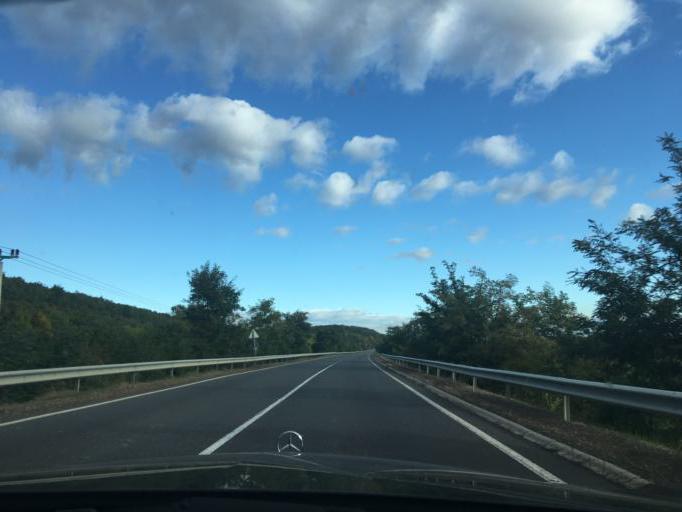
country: HU
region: Borsod-Abauj-Zemplen
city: Gonc
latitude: 48.4409
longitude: 21.1846
